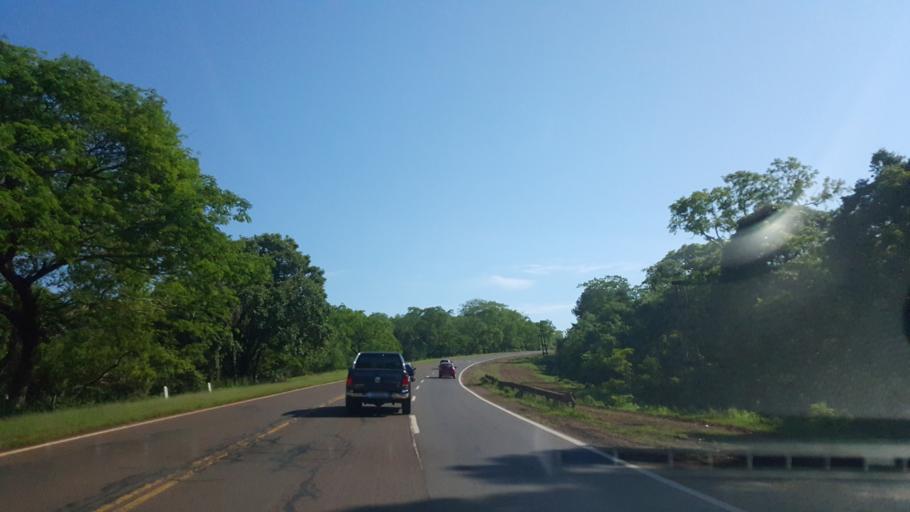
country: AR
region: Misiones
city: Santa Ana
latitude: -27.3596
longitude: -55.5572
